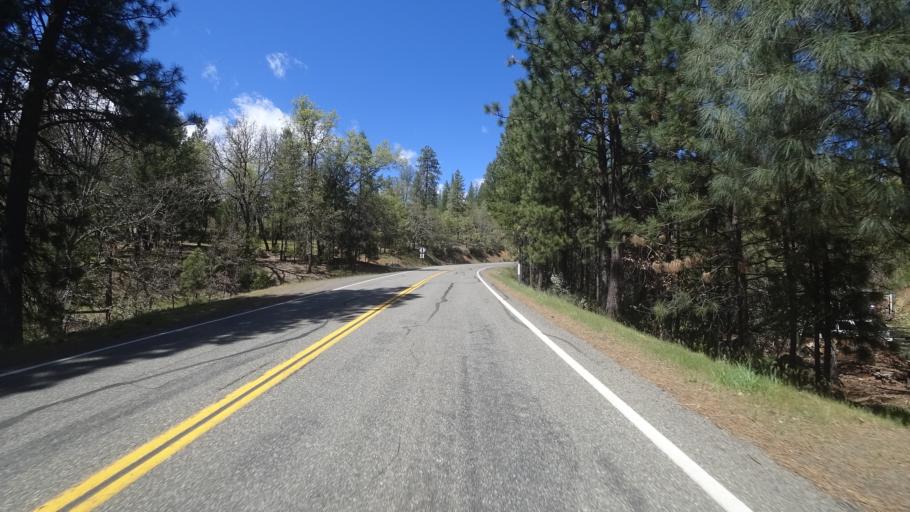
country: US
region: California
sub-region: Trinity County
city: Weaverville
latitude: 40.7541
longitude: -122.9131
